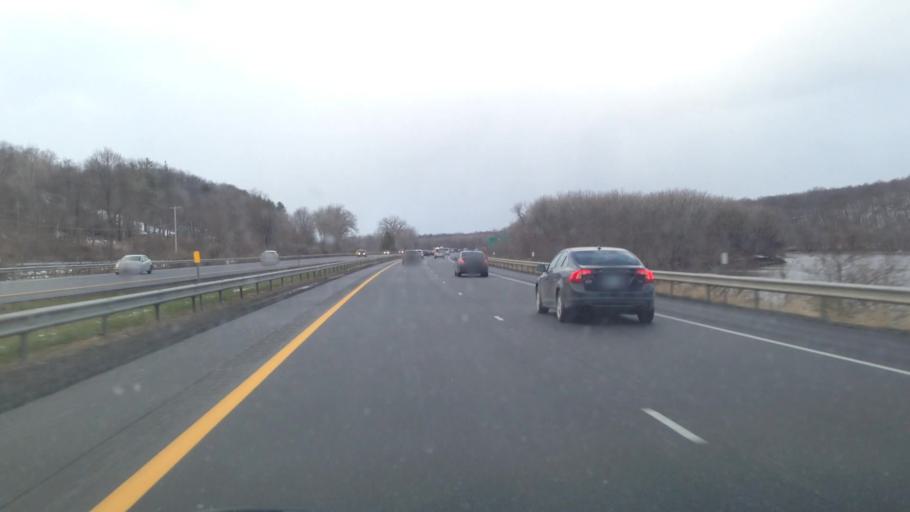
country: US
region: New York
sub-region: Montgomery County
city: Canajoharie
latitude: 42.8975
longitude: -74.5394
